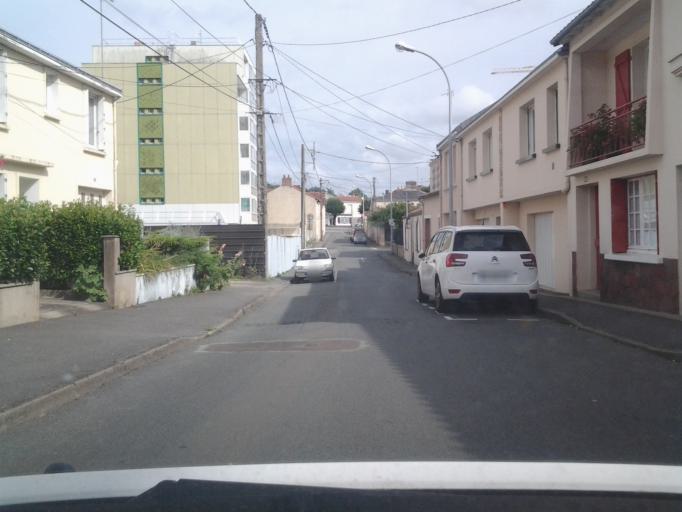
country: FR
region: Pays de la Loire
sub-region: Departement de la Vendee
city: La Roche-sur-Yon
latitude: 46.6674
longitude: -1.4212
